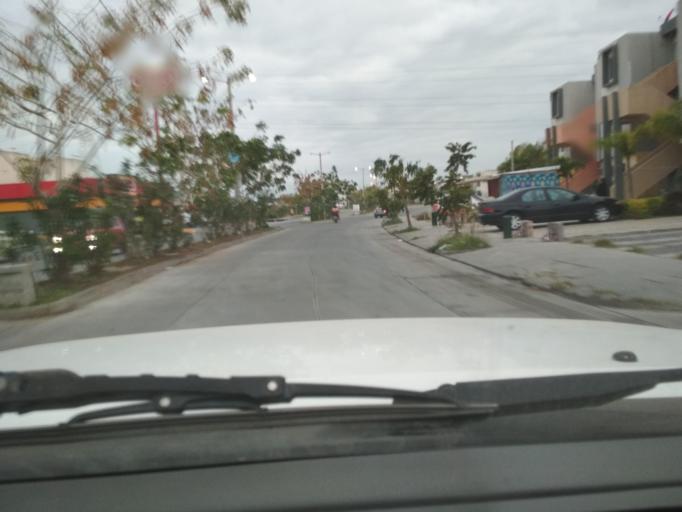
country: MX
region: Veracruz
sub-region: Medellin
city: Fraccionamiento Arboledas San Ramon
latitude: 19.0914
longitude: -96.1646
